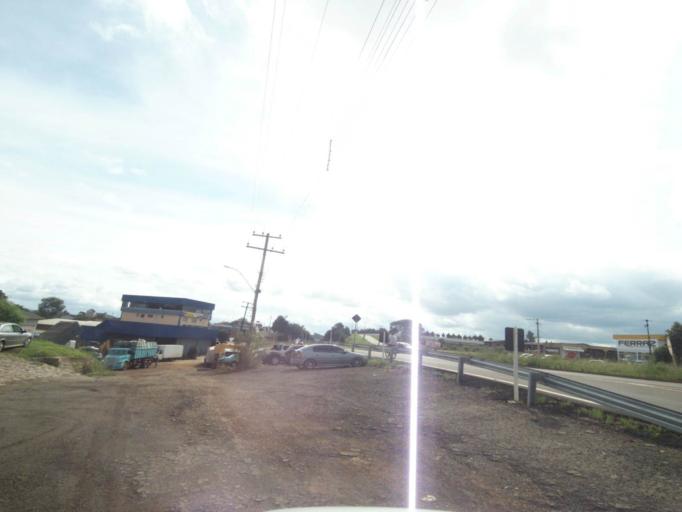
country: BR
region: Rio Grande do Sul
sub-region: Lagoa Vermelha
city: Lagoa Vermelha
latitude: -28.2044
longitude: -51.5299
